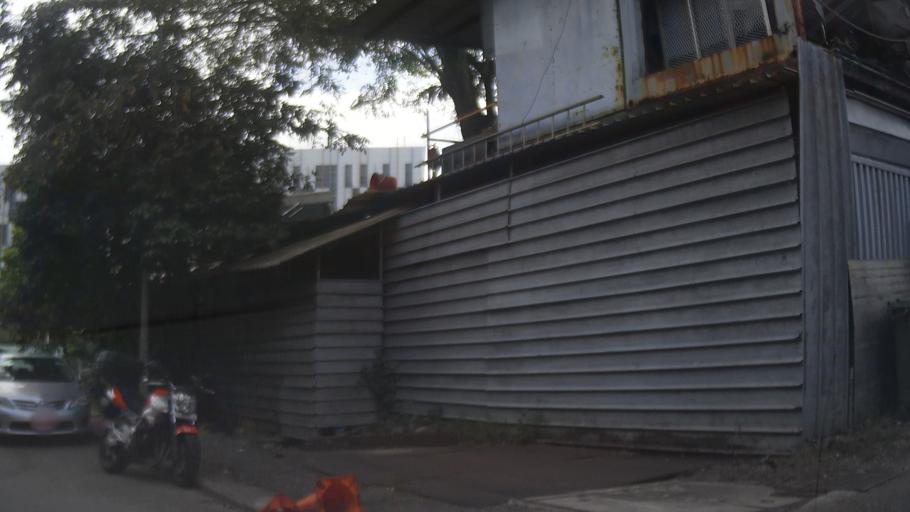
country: MY
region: Johor
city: Johor Bahru
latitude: 1.4050
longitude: 103.7575
